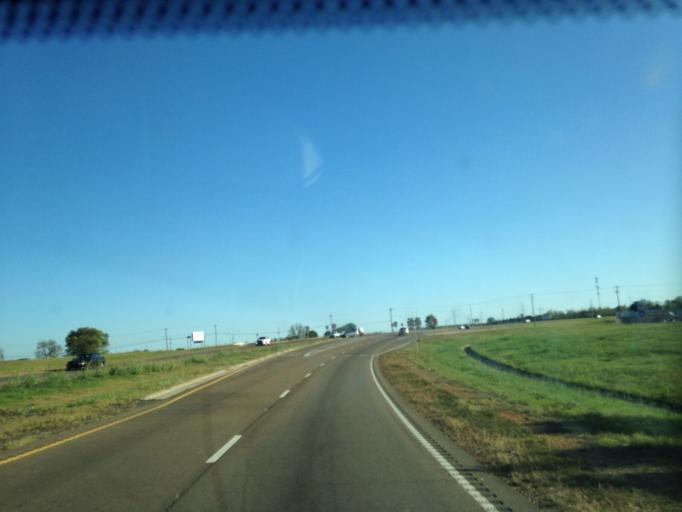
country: US
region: Mississippi
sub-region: Lowndes County
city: Columbus
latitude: 33.4811
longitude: -88.4893
